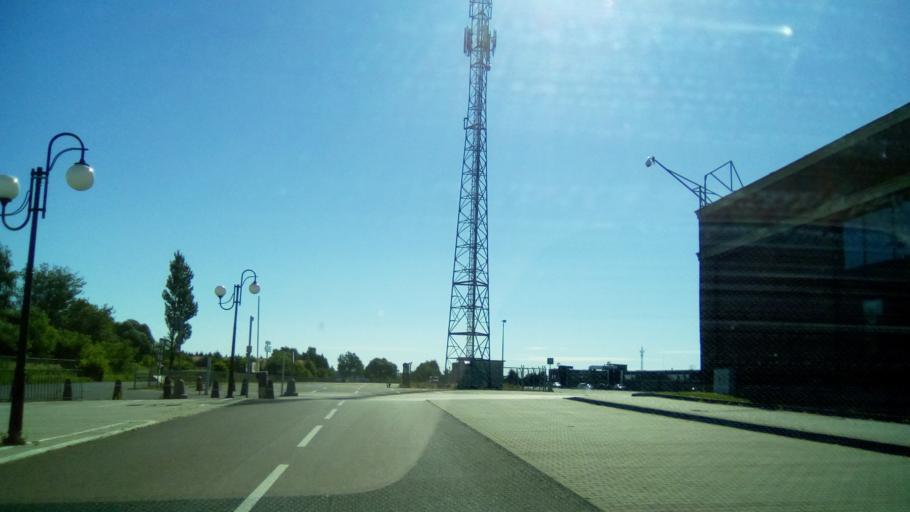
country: PL
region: Lodz Voivodeship
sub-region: Powiat lodzki wschodni
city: Rzgow
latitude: 51.6511
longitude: 19.4878
